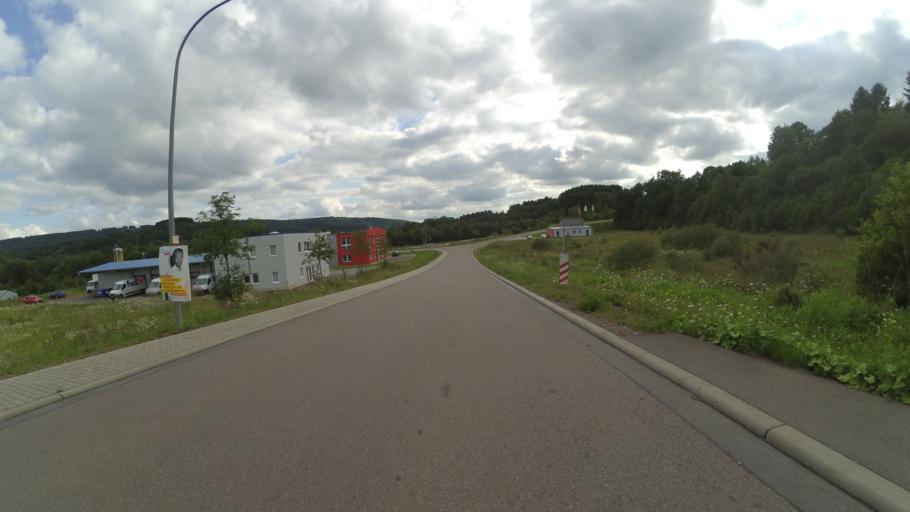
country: DE
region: Rheinland-Pfalz
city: Neuhutten
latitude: 49.5987
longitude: 6.9969
